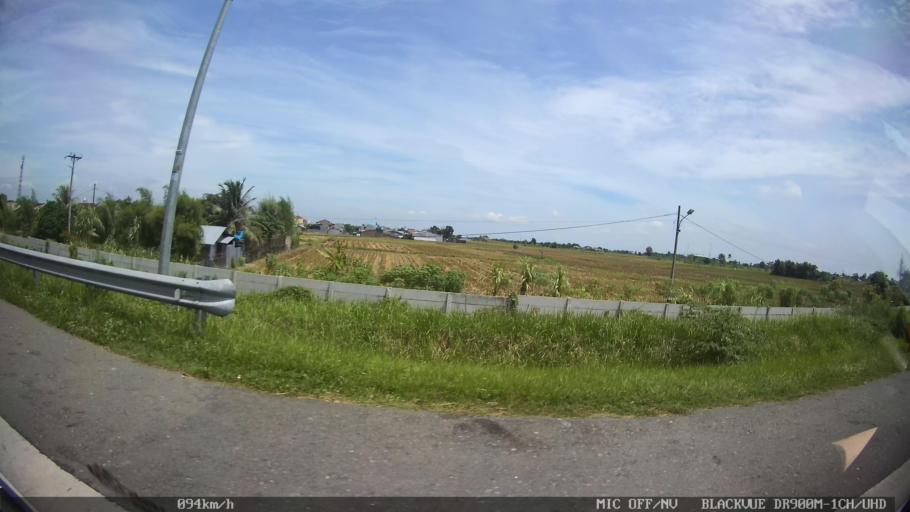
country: ID
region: North Sumatra
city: Perbaungan
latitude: 3.5320
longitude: 98.8892
